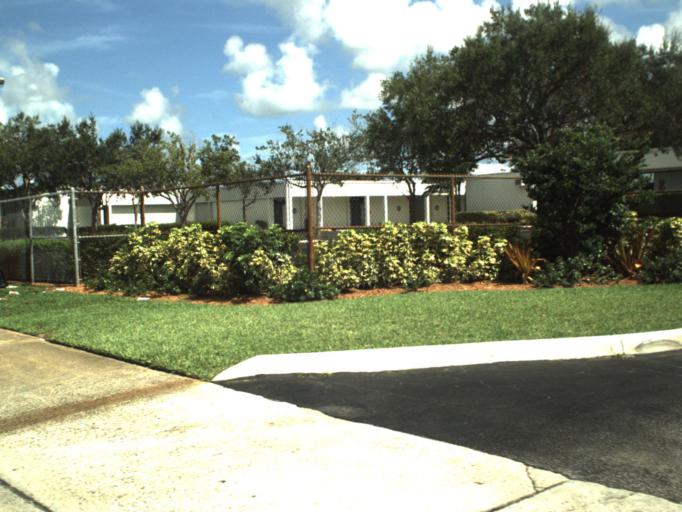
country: US
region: Florida
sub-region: Broward County
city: Pembroke Pines
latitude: 26.0325
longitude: -80.1983
